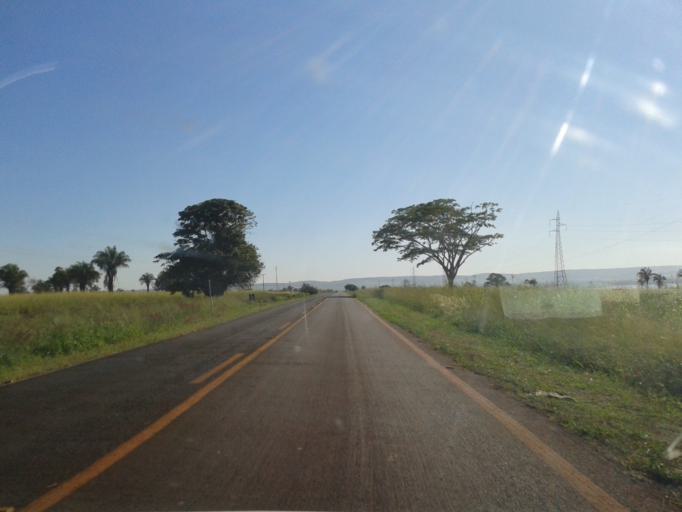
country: BR
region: Minas Gerais
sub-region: Capinopolis
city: Capinopolis
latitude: -18.5365
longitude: -49.5023
